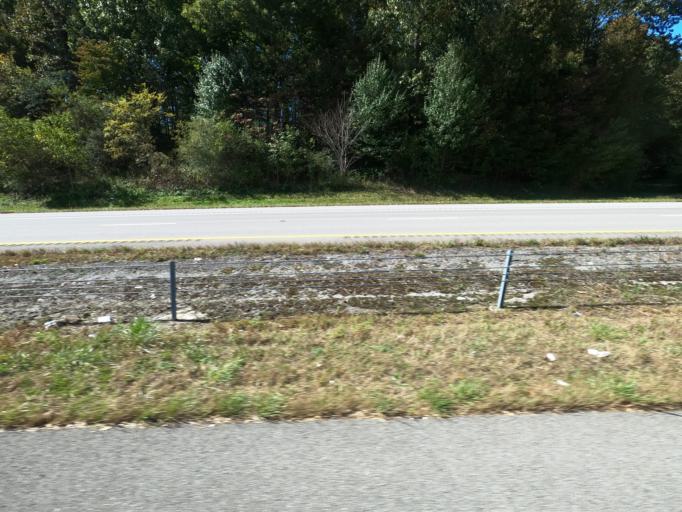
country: US
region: Tennessee
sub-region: Maury County
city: Mount Pleasant
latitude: 35.4129
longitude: -87.2818
